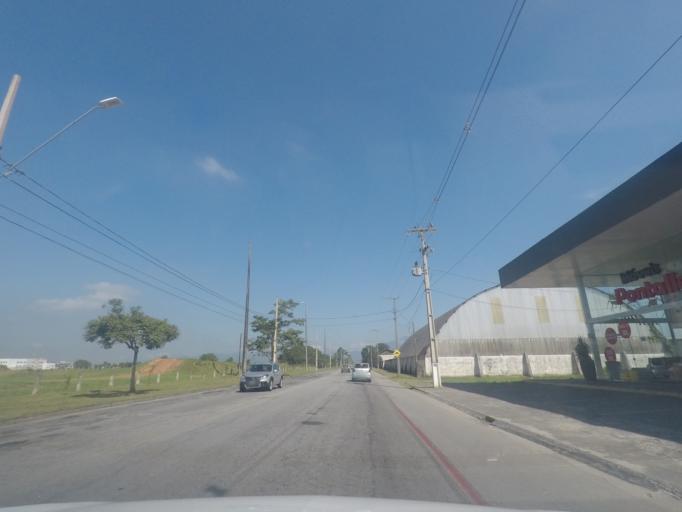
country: BR
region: Parana
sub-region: Paranagua
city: Paranagua
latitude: -25.5381
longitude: -48.5314
